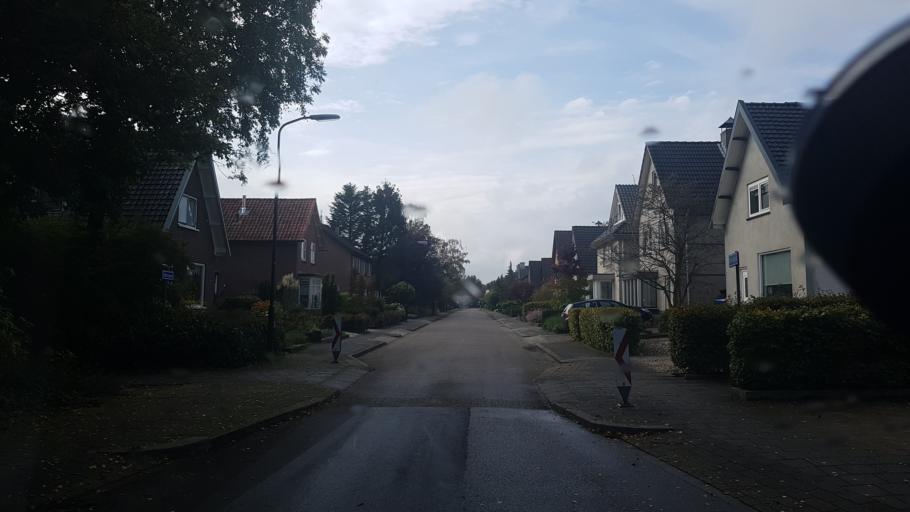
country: NL
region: Gelderland
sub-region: Gemeente Apeldoorn
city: Beekbergen
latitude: 52.1854
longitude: 5.9486
